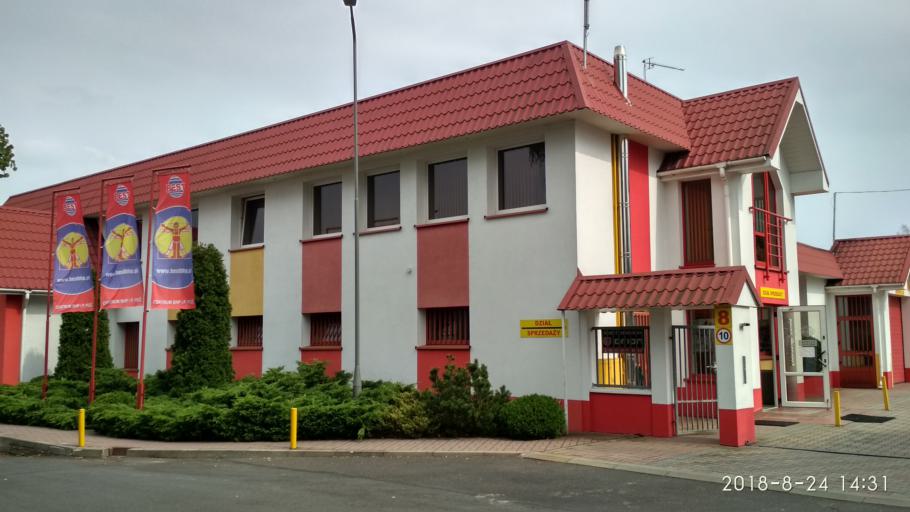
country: PL
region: Lubusz
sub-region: Zielona Gora
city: Zielona Gora
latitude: 51.9527
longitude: 15.4654
